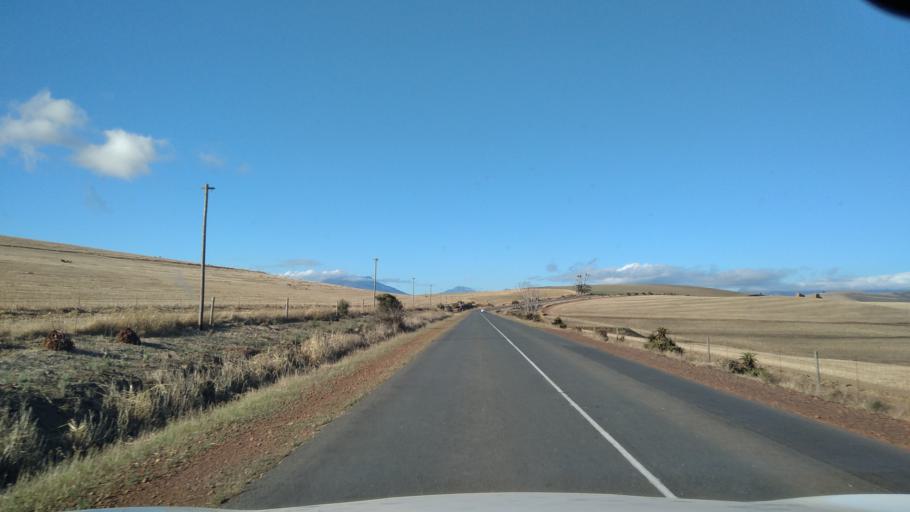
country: ZA
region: Western Cape
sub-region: Overberg District Municipality
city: Caledon
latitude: -34.1925
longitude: 19.2700
